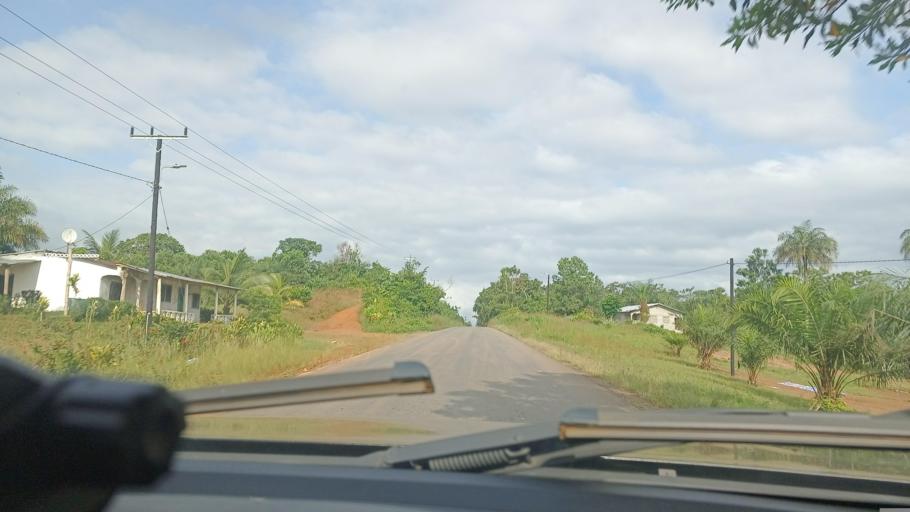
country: LR
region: Bomi
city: Tubmanburg
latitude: 6.7085
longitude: -10.9298
